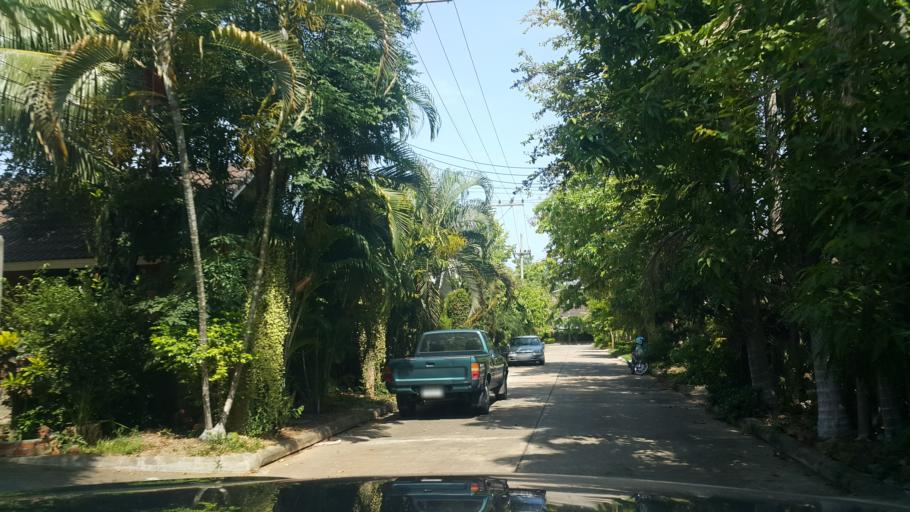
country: TH
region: Chiang Mai
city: Chiang Mai
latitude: 18.7292
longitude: 98.9699
